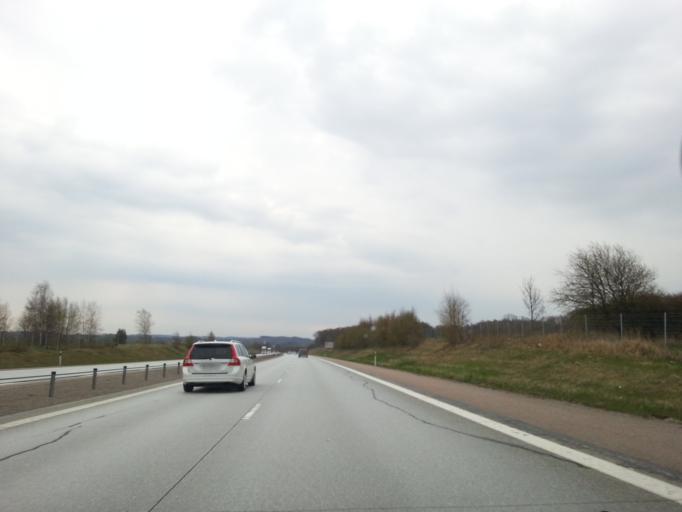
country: SE
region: Halland
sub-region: Halmstads Kommun
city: Getinge
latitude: 56.8683
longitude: 12.6465
